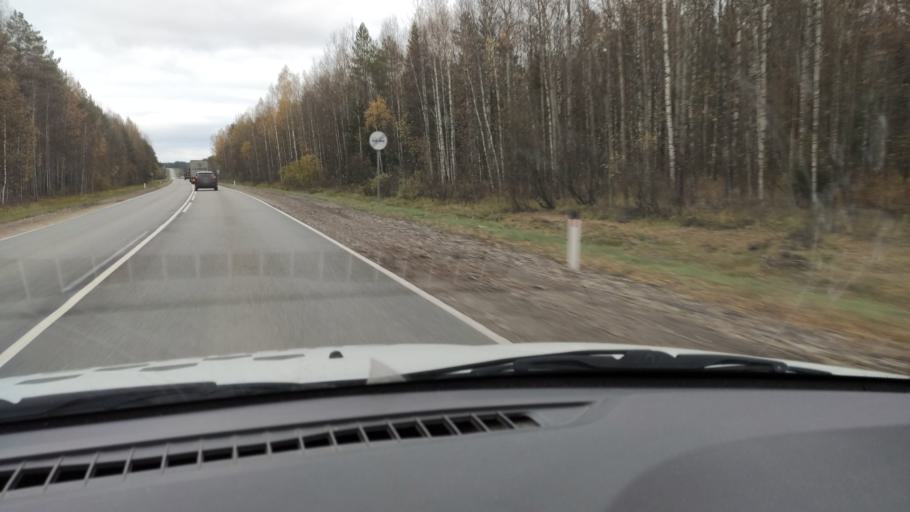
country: RU
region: Kirov
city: Slobodskoy
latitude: 58.7282
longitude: 50.2501
